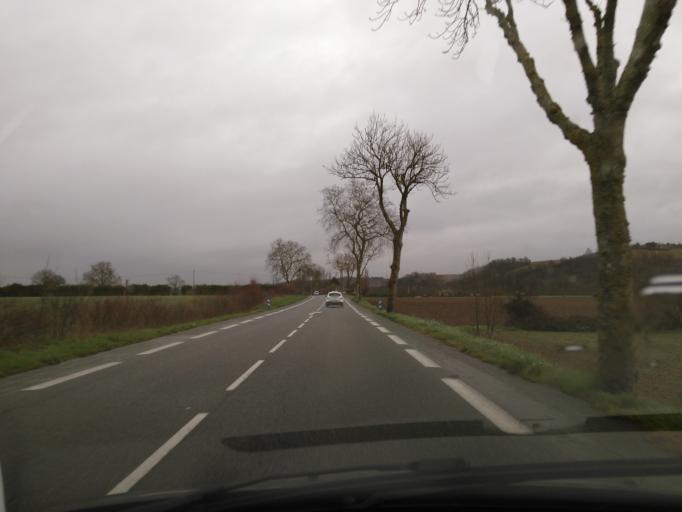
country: FR
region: Midi-Pyrenees
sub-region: Departement de la Haute-Garonne
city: Carbonne
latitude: 43.2774
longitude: 1.2080
